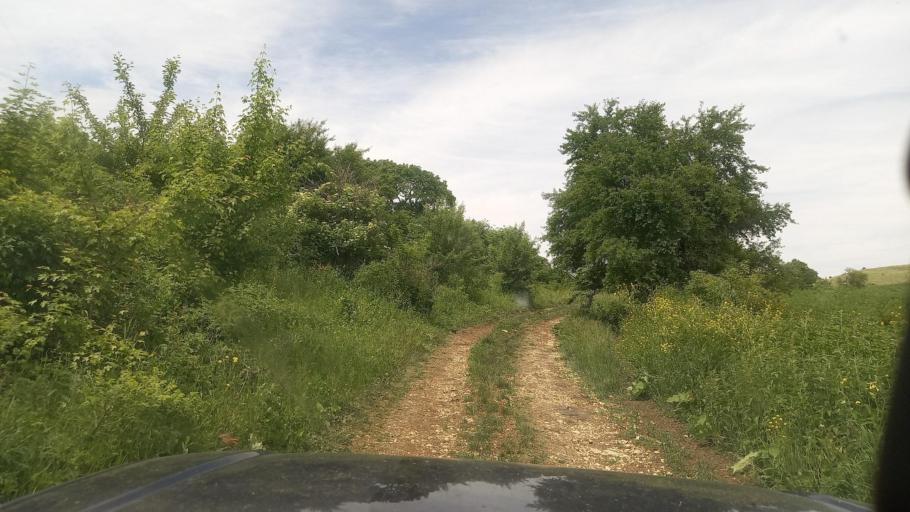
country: RU
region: Karachayevo-Cherkesiya
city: Pregradnaya
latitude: 44.0944
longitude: 41.1672
